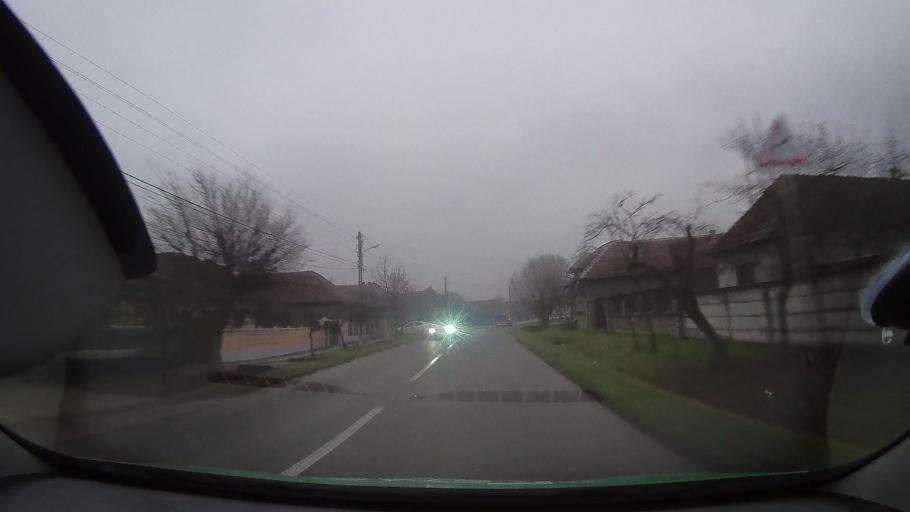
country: RO
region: Bihor
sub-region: Comuna Tulca
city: Tulca
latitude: 46.7917
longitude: 21.7705
